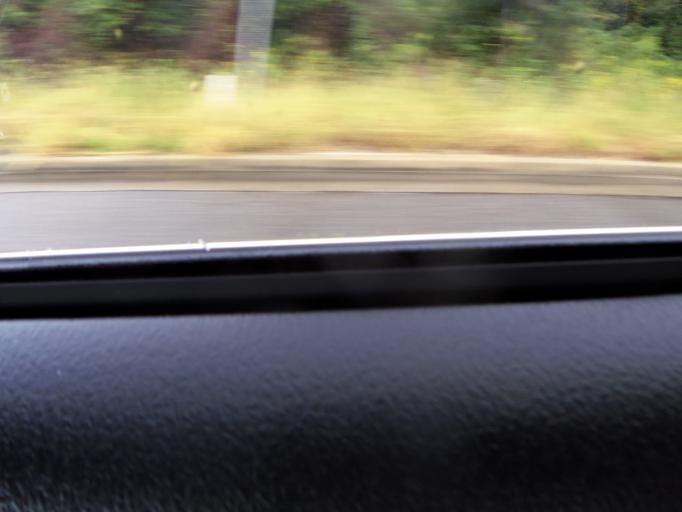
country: US
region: Georgia
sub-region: Wayne County
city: Jesup
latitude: 31.6466
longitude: -81.8561
